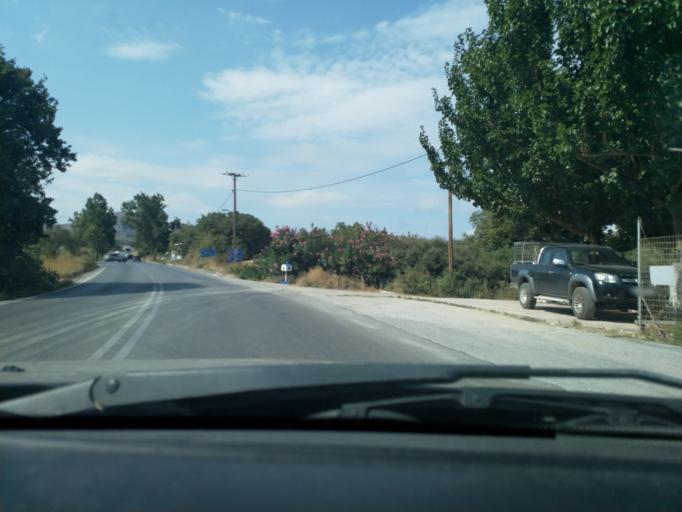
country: GR
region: Crete
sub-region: Nomos Rethymnis
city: Atsipopoulon
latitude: 35.2301
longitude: 24.4746
